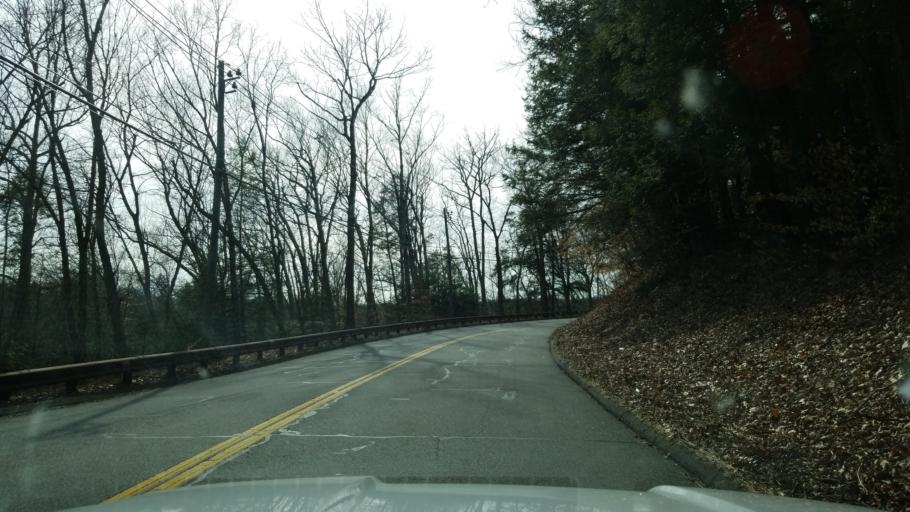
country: US
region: Connecticut
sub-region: Hartford County
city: Glastonbury Center
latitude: 41.6622
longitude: -72.5877
